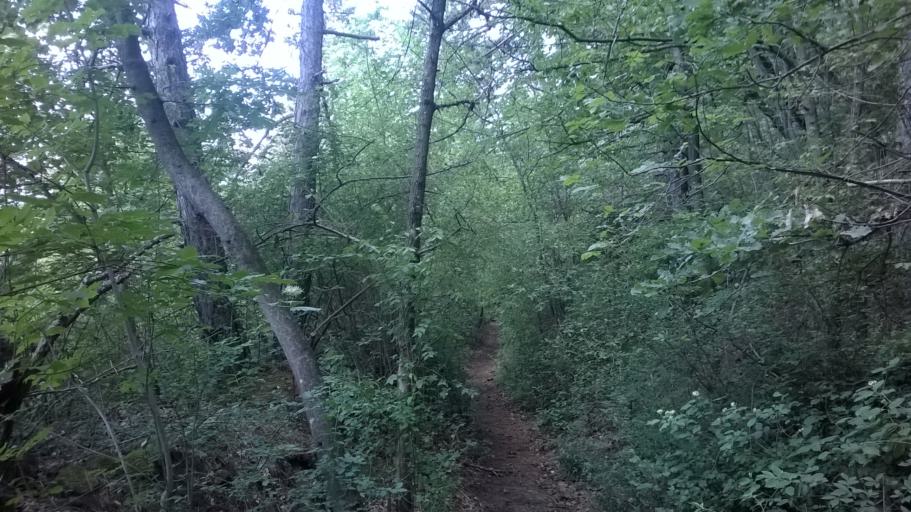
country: HU
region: Pest
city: Pilisborosjeno
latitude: 47.6105
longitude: 19.0024
